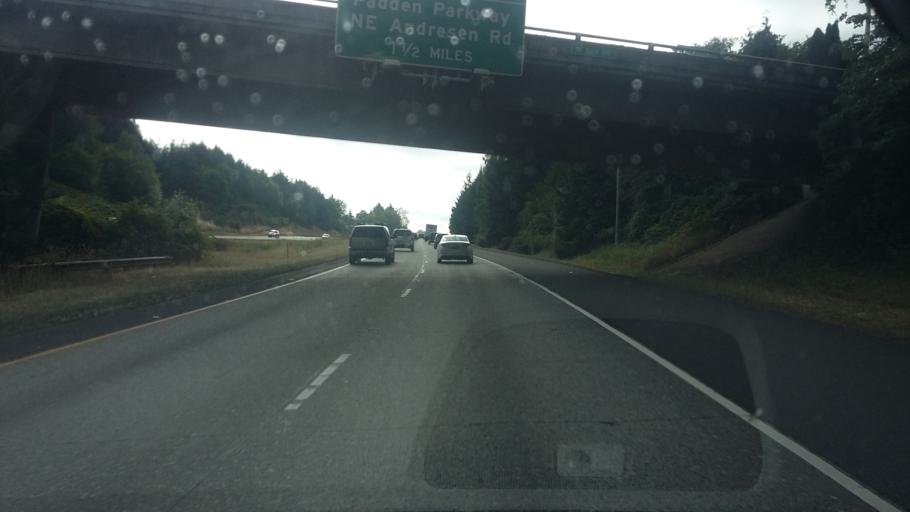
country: US
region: Washington
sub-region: Clark County
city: Barberton
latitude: 45.6992
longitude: -122.6211
